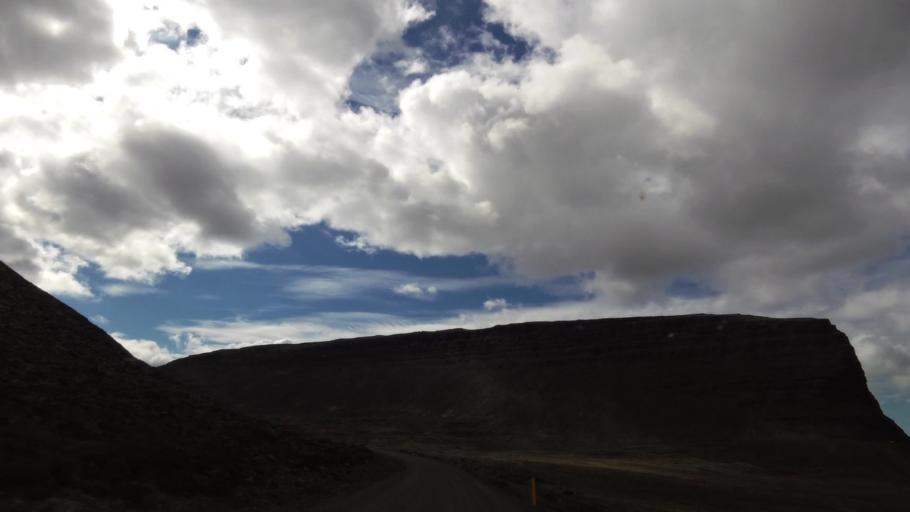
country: IS
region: West
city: Olafsvik
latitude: 65.5766
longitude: -24.0723
